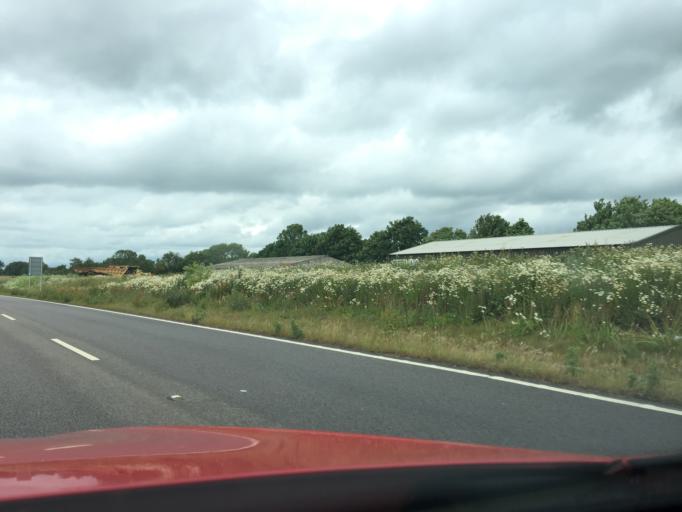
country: GB
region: England
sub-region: Northamptonshire
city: Bugbrooke
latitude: 52.2312
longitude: -1.0254
